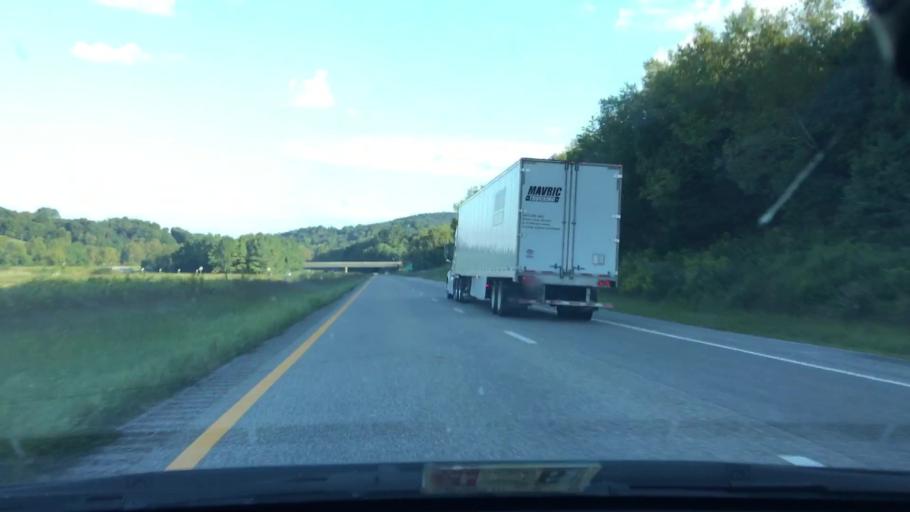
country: US
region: Virginia
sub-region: City of Lexington
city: Lexington
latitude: 37.8566
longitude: -79.4833
